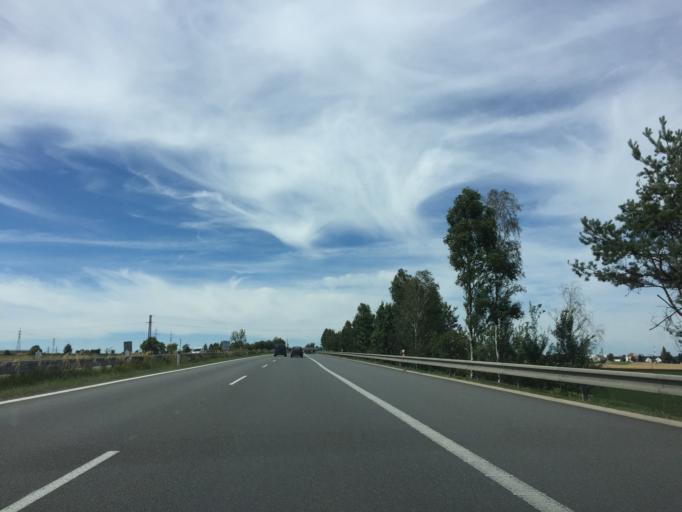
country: CZ
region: Jihocesky
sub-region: Okres Tabor
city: Sezimovo Usti
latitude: 49.4132
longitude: 14.7110
